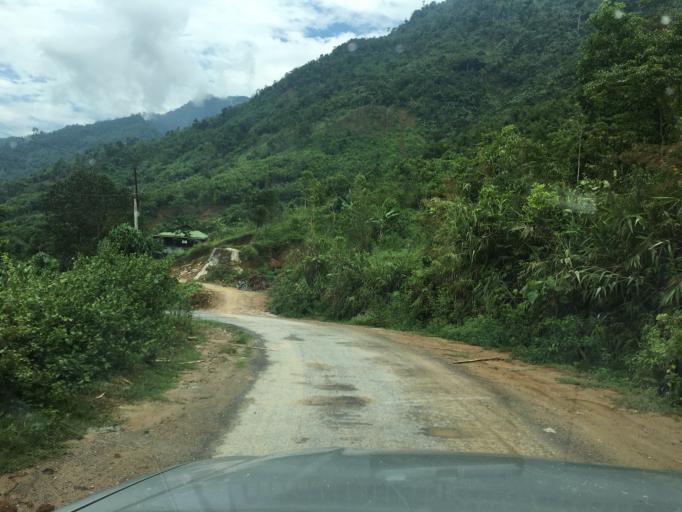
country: VN
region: Yen Bai
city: Son Thinh
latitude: 21.6831
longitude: 104.5752
